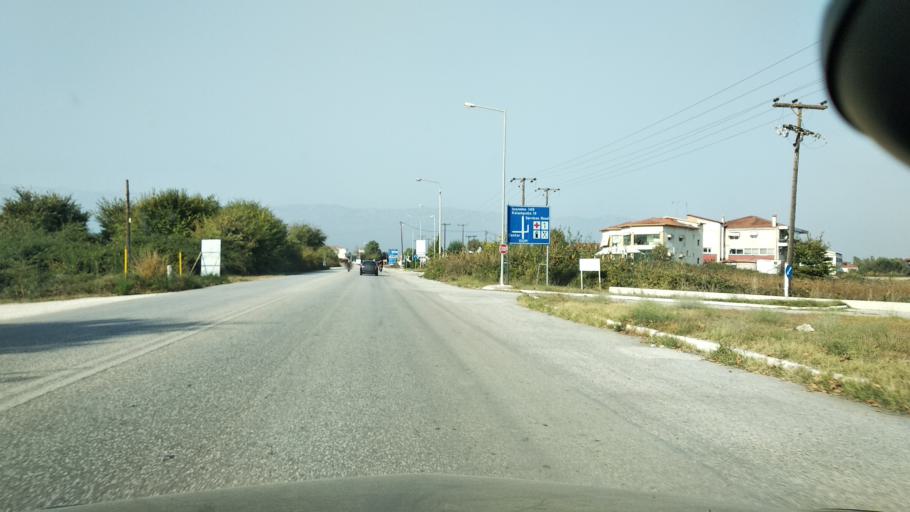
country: GR
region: Thessaly
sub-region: Trikala
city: Pyrgetos
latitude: 39.5712
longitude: 21.7526
